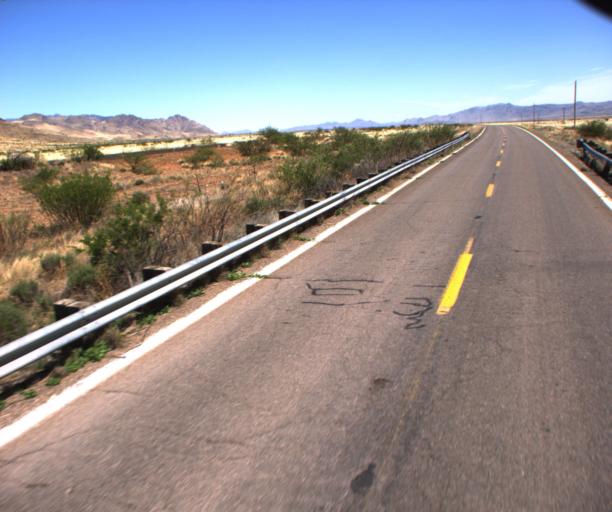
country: US
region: Arizona
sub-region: Cochise County
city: Douglas
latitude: 31.6515
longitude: -109.1611
